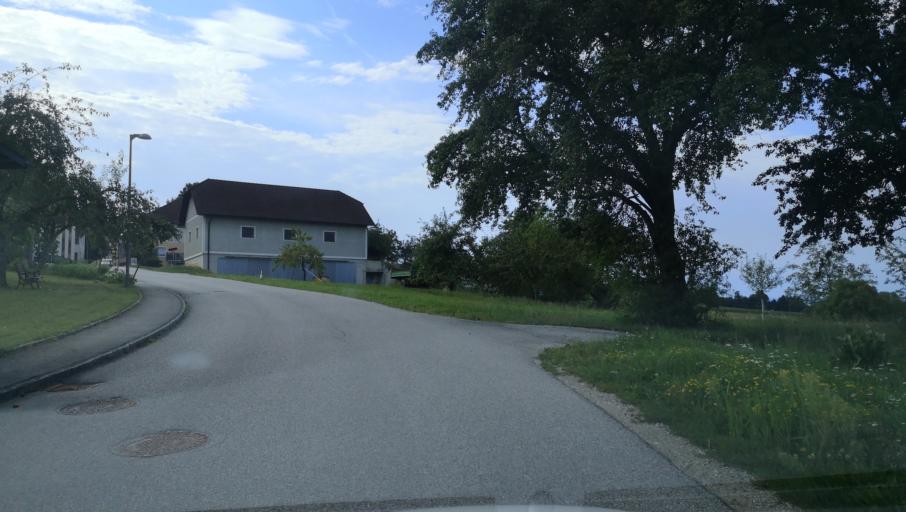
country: AT
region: Lower Austria
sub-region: Politischer Bezirk Amstetten
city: Zeillern
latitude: 48.1583
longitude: 14.8207
